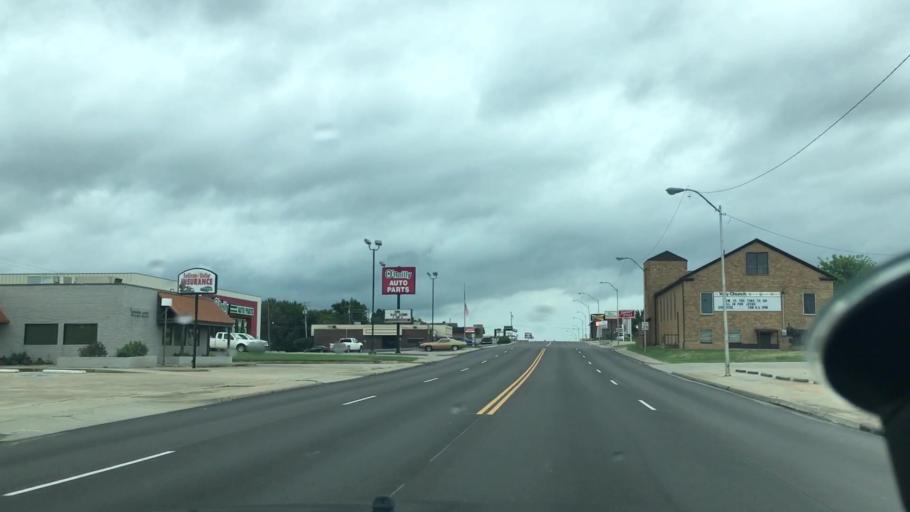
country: US
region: Oklahoma
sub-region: Seminole County
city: Seminole
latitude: 35.2310
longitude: -96.6711
